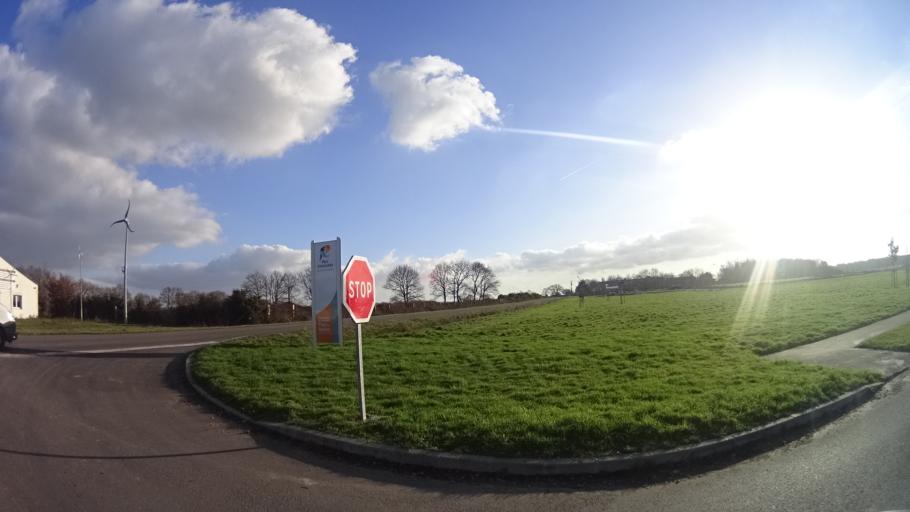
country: FR
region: Pays de la Loire
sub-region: Departement de la Loire-Atlantique
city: Plesse
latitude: 47.5270
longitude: -1.8865
